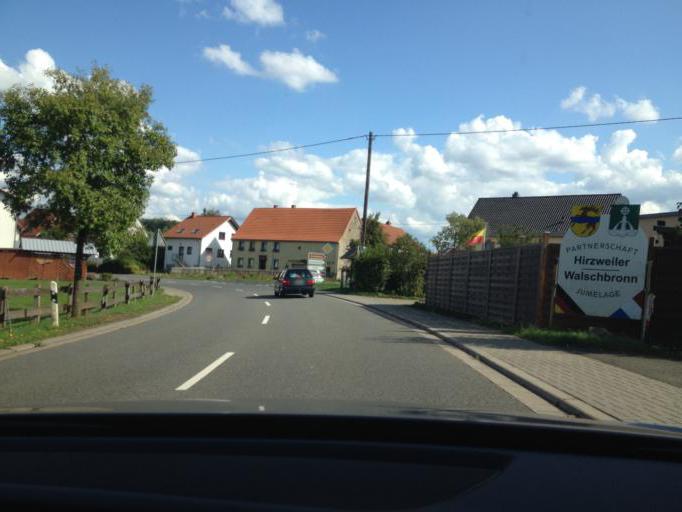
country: DE
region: Saarland
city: Mainzweiler
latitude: 49.4036
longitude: 7.0789
